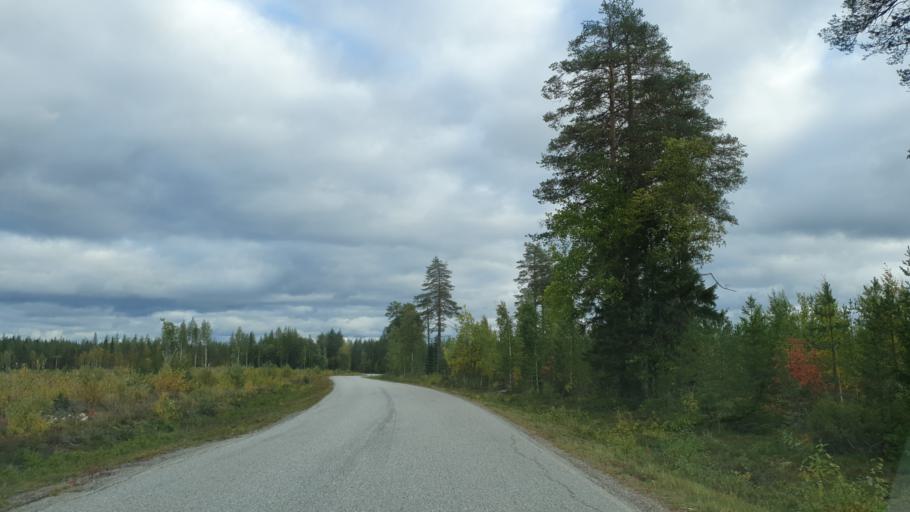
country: FI
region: Kainuu
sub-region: Kehys-Kainuu
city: Kuhmo
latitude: 63.9494
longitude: 29.7561
